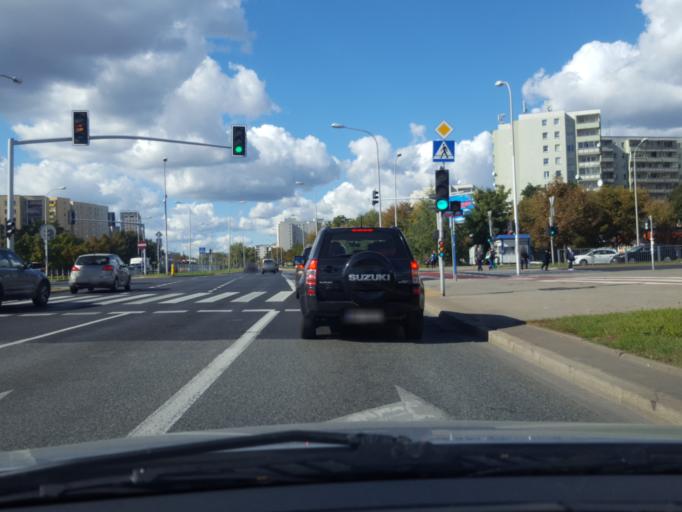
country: PL
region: Masovian Voivodeship
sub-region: Warszawa
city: Praga Poludnie
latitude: 52.2229
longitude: 21.1019
